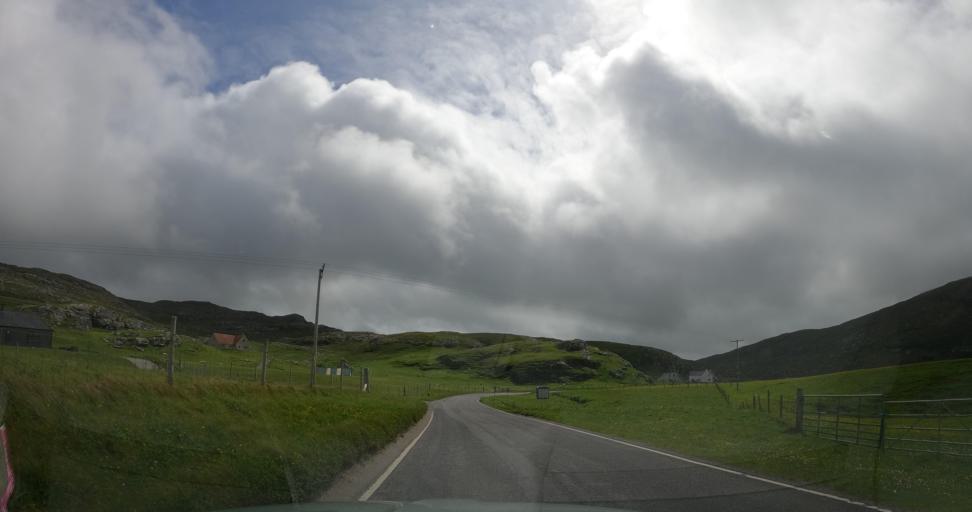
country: GB
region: Scotland
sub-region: Eilean Siar
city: Barra
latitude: 56.9729
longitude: -7.5159
